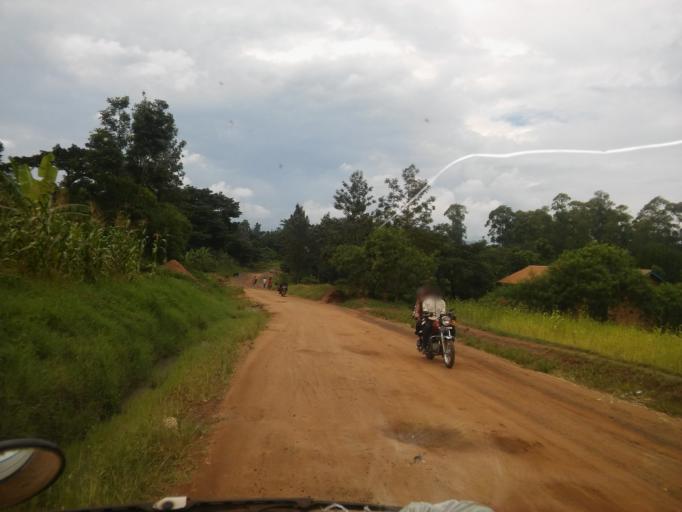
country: UG
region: Eastern Region
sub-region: Bududa District
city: Bududa
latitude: 0.9506
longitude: 34.2633
